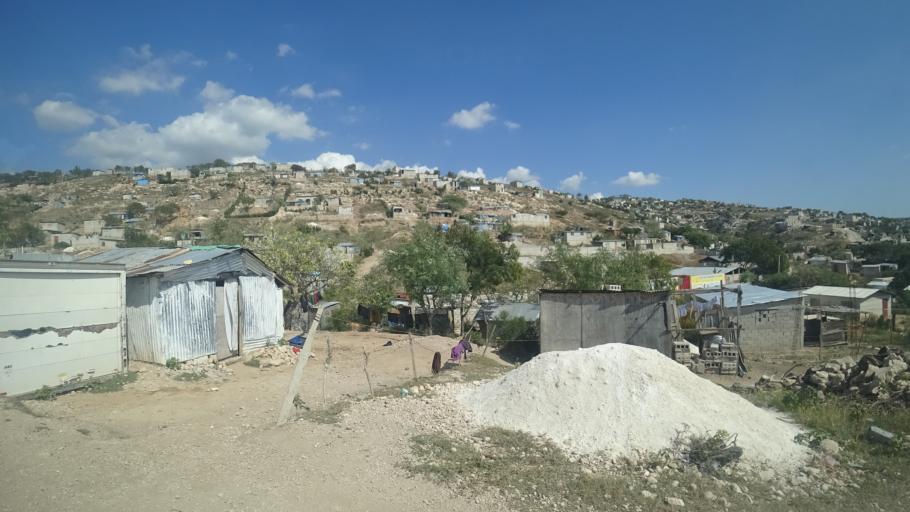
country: HT
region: Ouest
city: Croix des Bouquets
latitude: 18.6602
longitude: -72.2857
